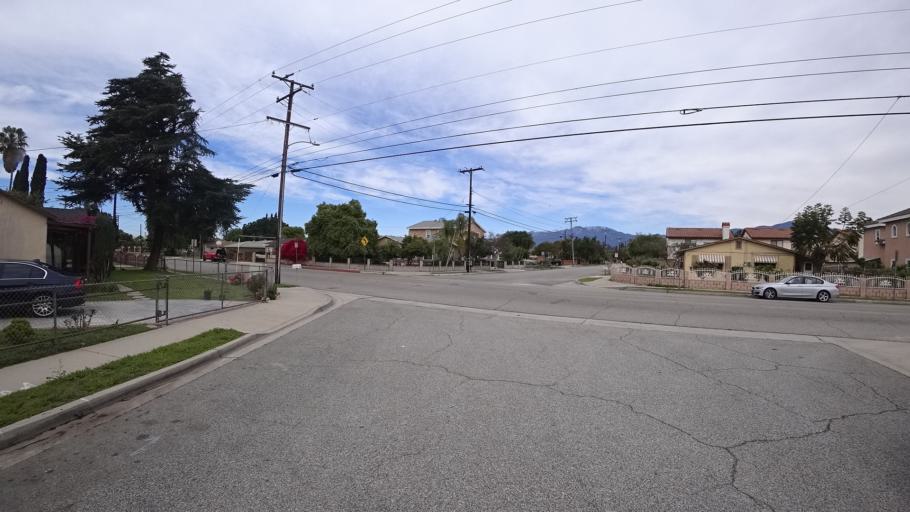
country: US
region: California
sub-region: Los Angeles County
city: Baldwin Park
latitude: 34.0784
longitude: -117.9776
